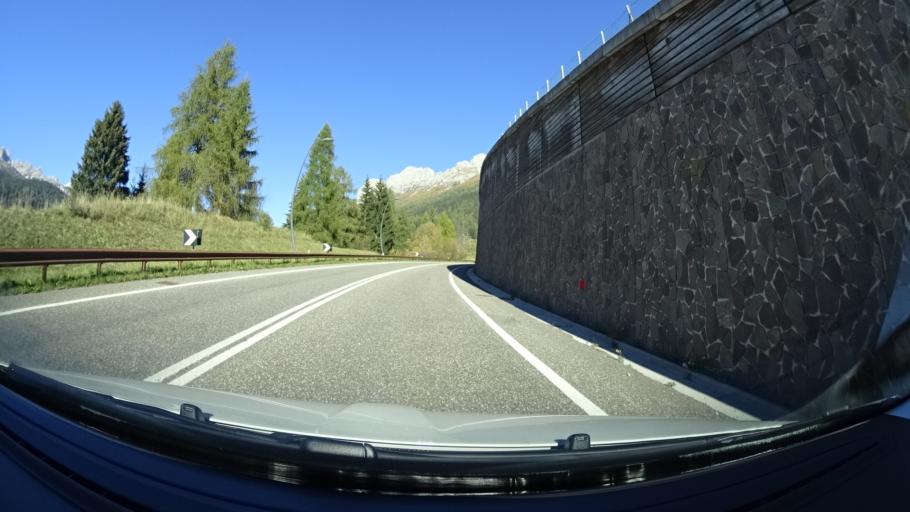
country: IT
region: Trentino-Alto Adige
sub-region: Provincia di Trento
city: Moena
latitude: 46.3720
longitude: 11.6598
